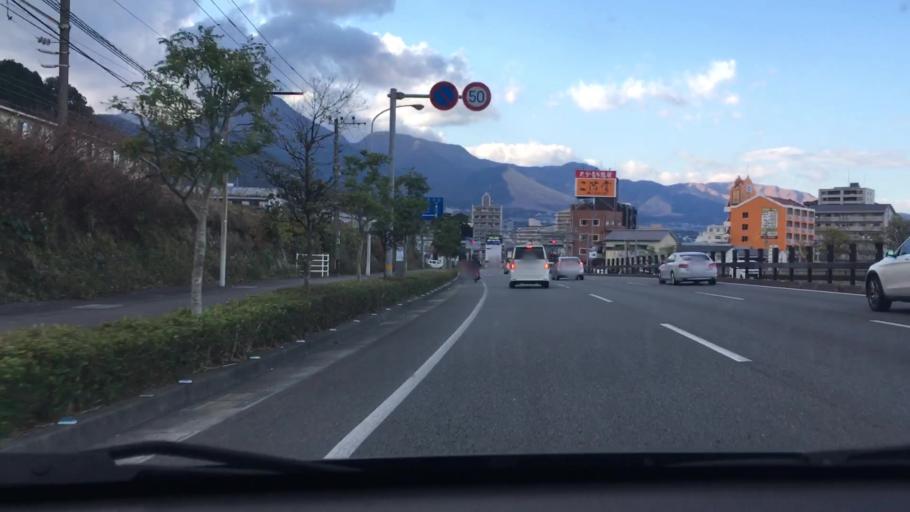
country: JP
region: Oita
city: Beppu
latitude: 33.2667
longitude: 131.5137
